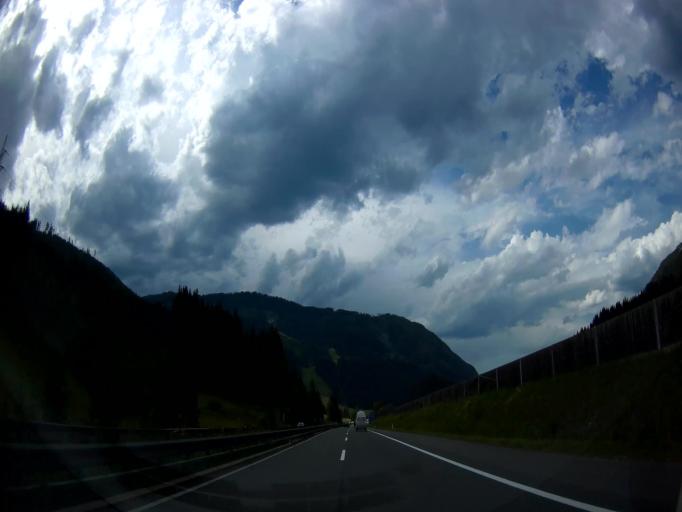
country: AT
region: Salzburg
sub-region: Politischer Bezirk Sankt Johann im Pongau
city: Flachau
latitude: 47.2896
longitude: 13.3990
